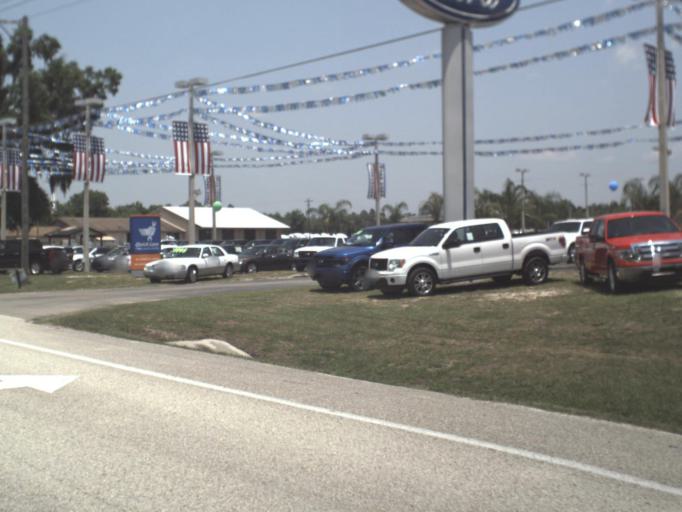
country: US
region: Florida
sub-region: Bradford County
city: Starke
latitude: 29.9059
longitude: -82.1355
